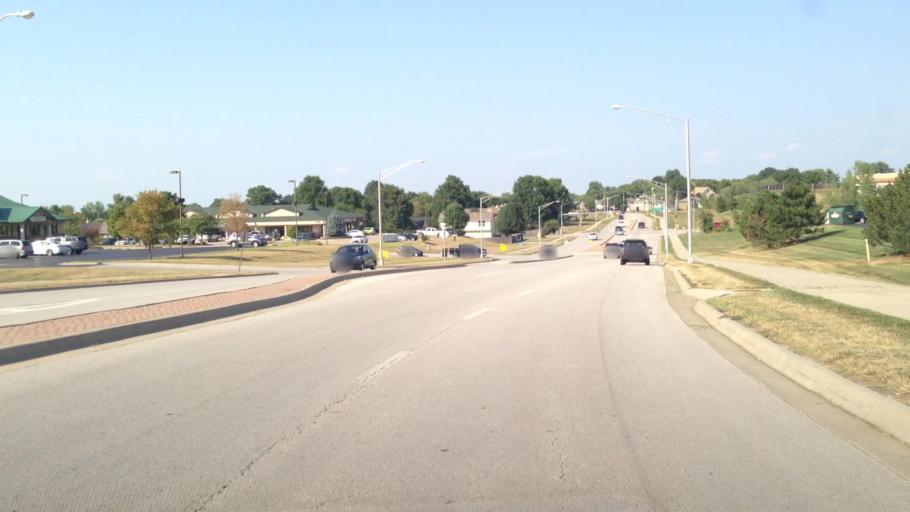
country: US
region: Kansas
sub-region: Wyandotte County
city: Edwardsville
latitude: 39.1272
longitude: -94.8322
